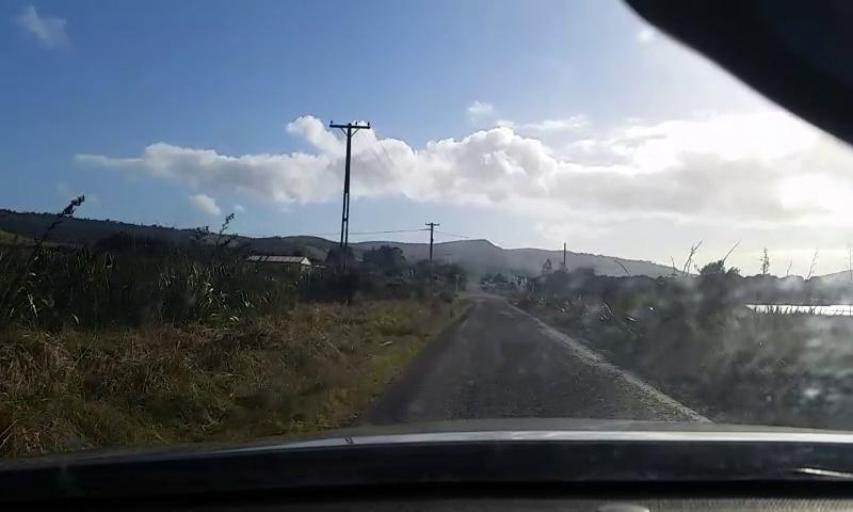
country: NZ
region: Otago
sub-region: Clutha District
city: Papatowai
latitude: -46.6272
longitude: 169.1360
